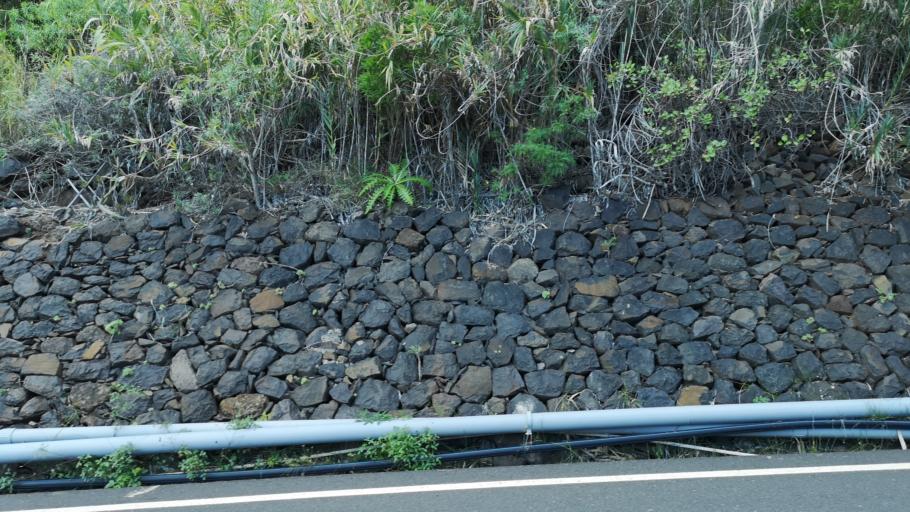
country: ES
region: Canary Islands
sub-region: Provincia de Santa Cruz de Tenerife
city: Agulo
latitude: 28.1888
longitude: -17.1982
